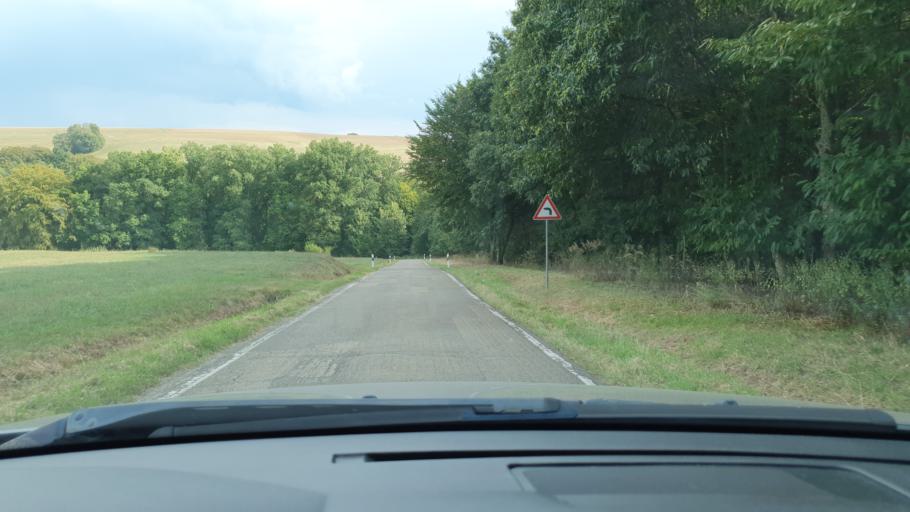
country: DE
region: Rheinland-Pfalz
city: Gerhardsbrunn
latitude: 49.3459
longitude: 7.5295
